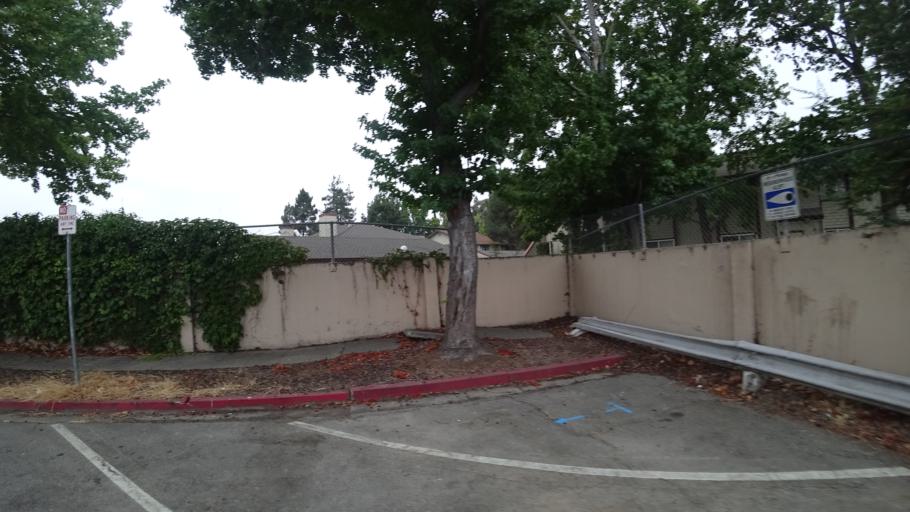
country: US
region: California
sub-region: Alameda County
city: Hayward
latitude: 37.6364
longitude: -122.0769
